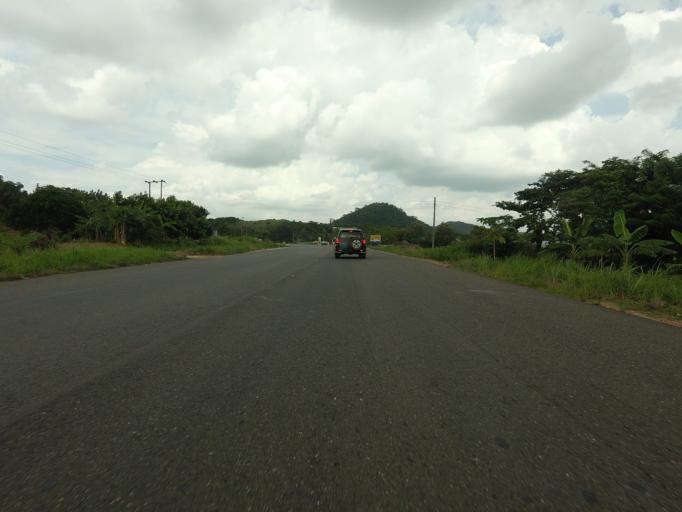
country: GH
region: Volta
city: Ho
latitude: 6.4301
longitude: 0.1687
